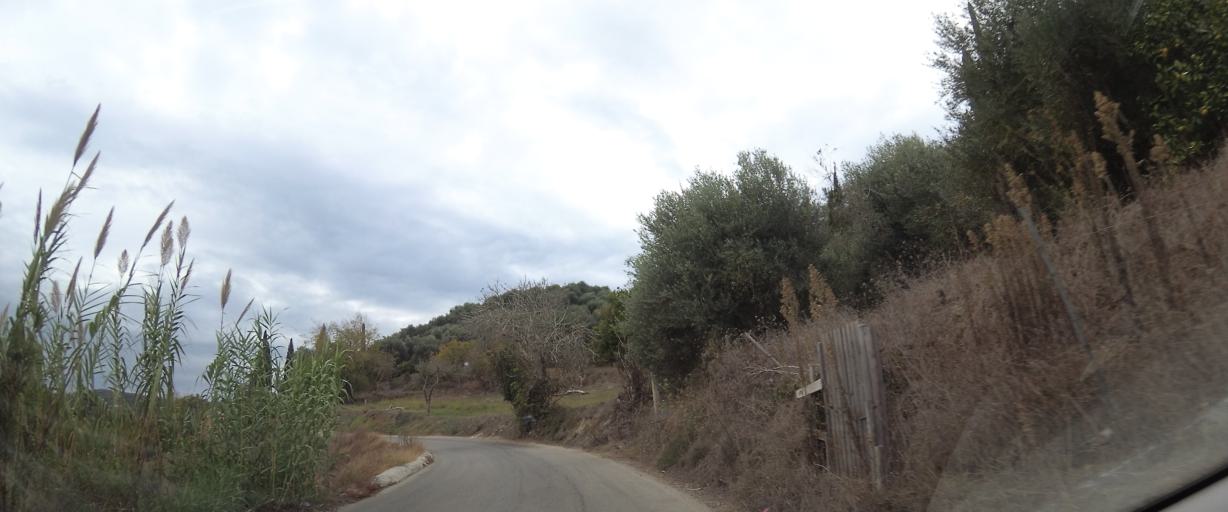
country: GR
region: Ionian Islands
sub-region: Nomos Kerkyras
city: Agios Georgis
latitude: 39.7560
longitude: 19.6881
